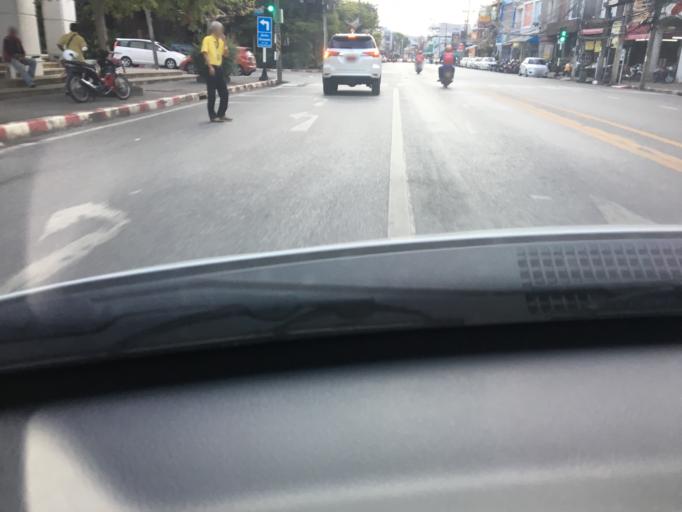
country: TH
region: Phuket
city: Ban Talat Yai
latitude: 7.8831
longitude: 98.3956
